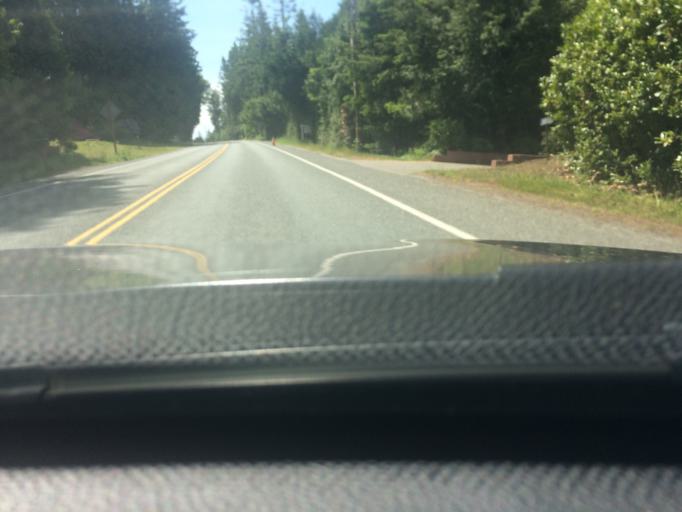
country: US
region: Washington
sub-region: Skagit County
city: Anacortes
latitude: 48.4392
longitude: -122.6642
